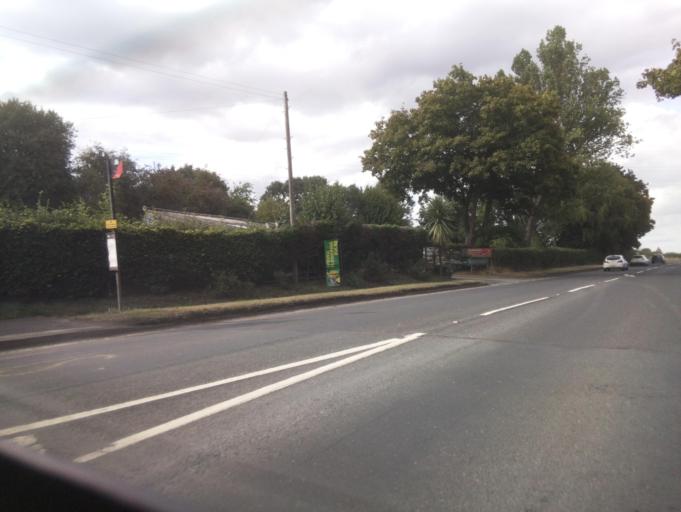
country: GB
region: England
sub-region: North Yorkshire
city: Ripon
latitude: 54.0658
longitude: -1.5382
